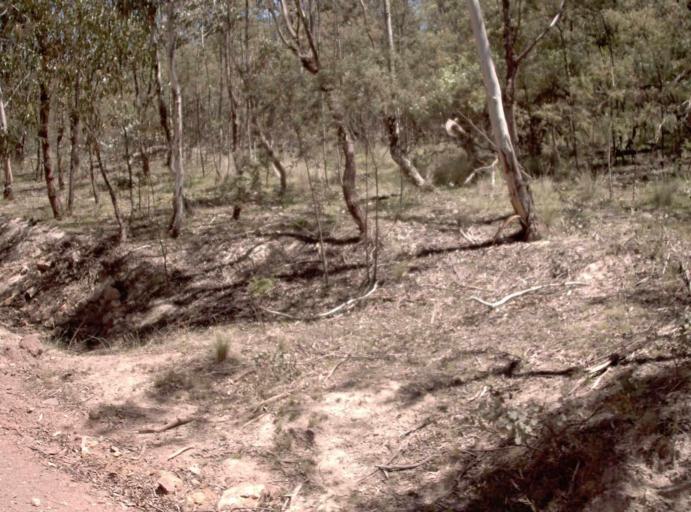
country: AU
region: New South Wales
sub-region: Snowy River
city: Jindabyne
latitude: -37.0650
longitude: 148.3185
